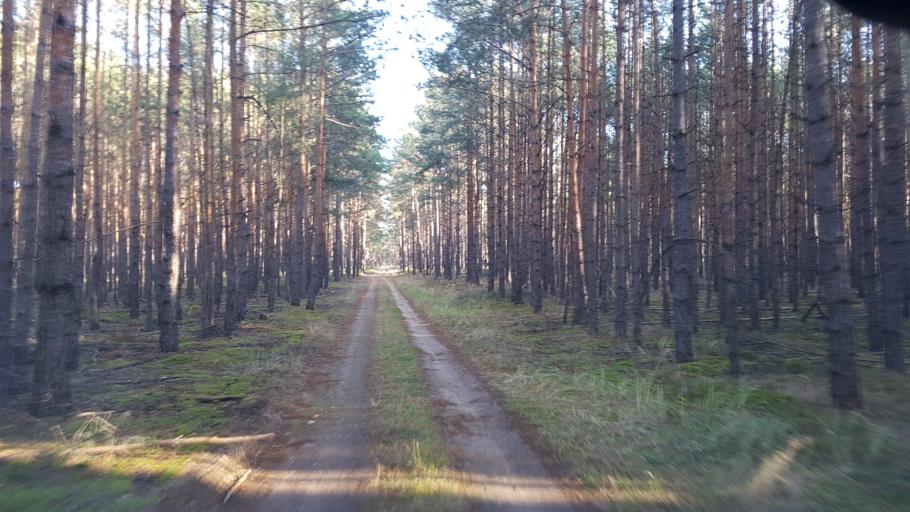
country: DE
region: Brandenburg
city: Sonnewalde
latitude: 51.6452
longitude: 13.6451
